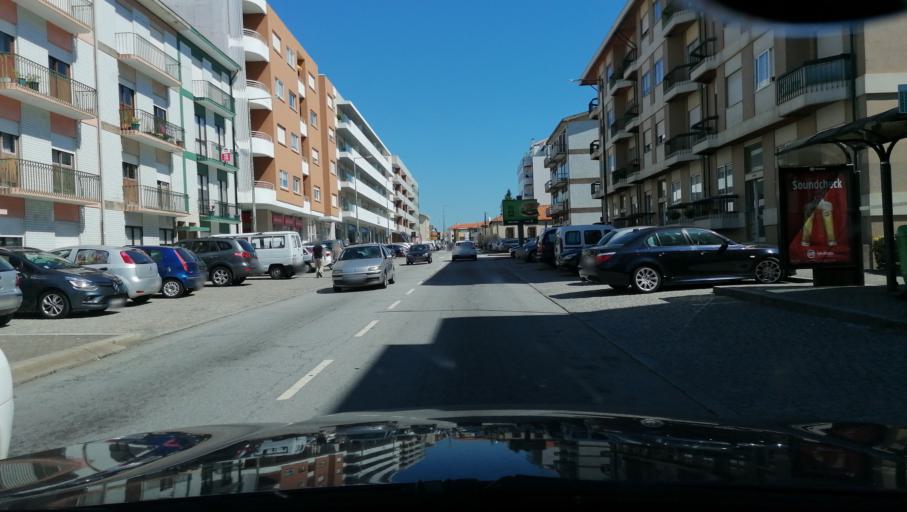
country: PT
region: Porto
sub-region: Vila Nova de Gaia
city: Canidelo
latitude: 41.1291
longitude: -8.6431
